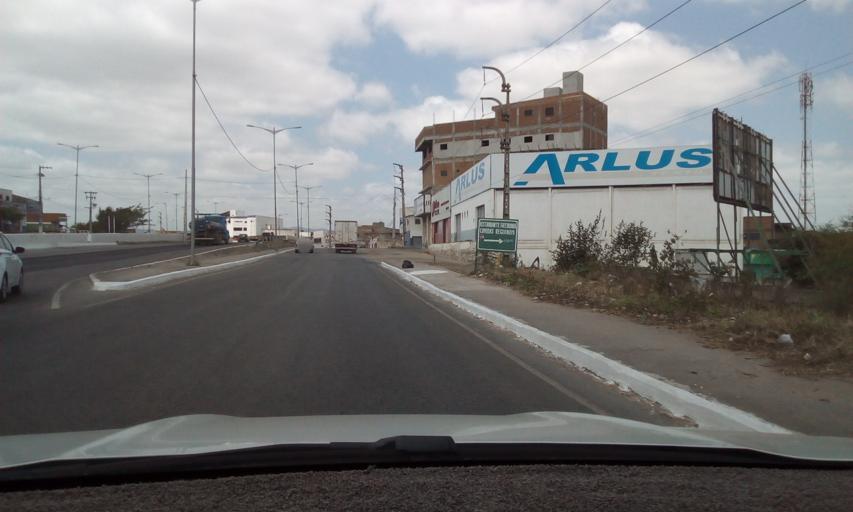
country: BR
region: Pernambuco
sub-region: Caruaru
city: Caruaru
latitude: -8.2712
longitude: -35.9815
